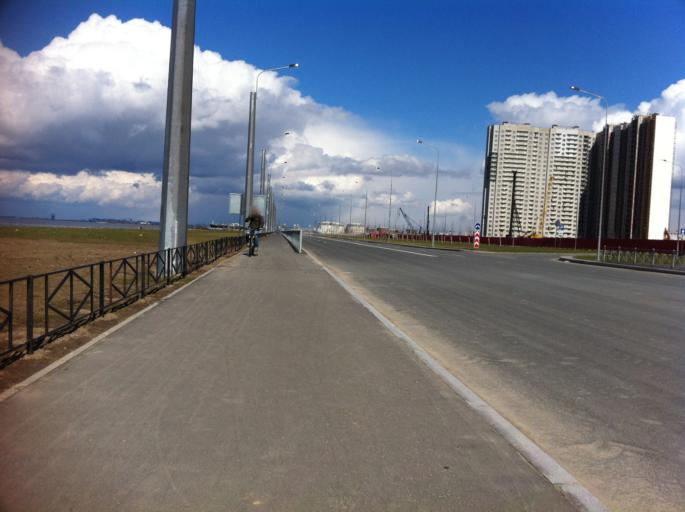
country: RU
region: St.-Petersburg
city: Sosnovaya Polyana
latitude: 59.8677
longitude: 30.1532
